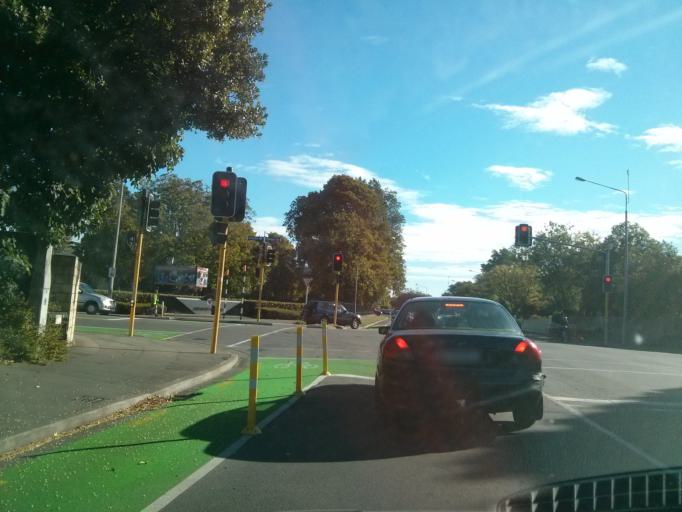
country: NZ
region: Canterbury
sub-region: Christchurch City
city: Christchurch
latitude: -43.5226
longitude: 172.5892
